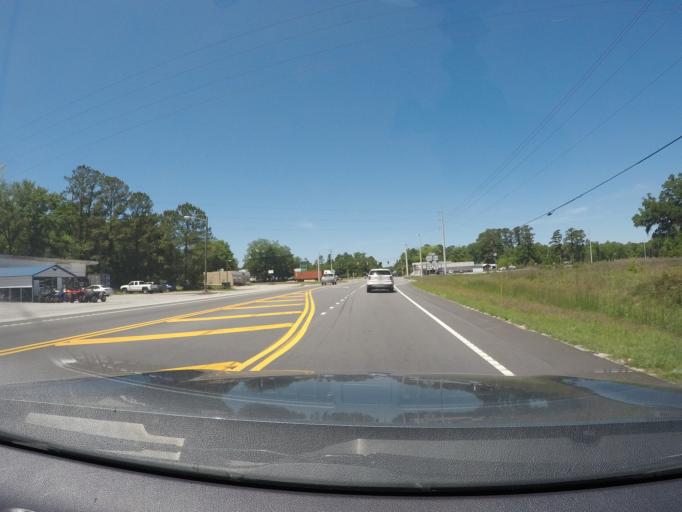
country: US
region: Georgia
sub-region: Effingham County
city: Guyton
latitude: 32.1965
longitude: -81.4367
